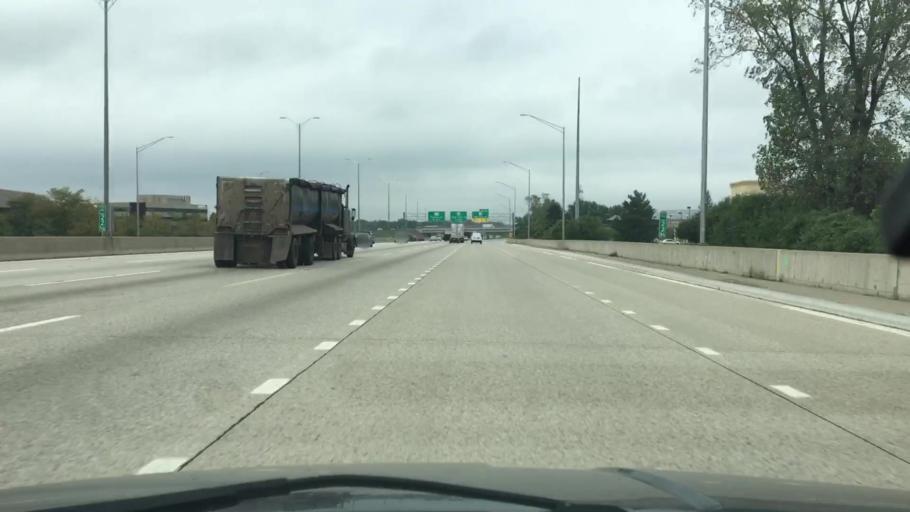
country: US
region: Illinois
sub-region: Lake County
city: Bannockburn
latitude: 42.1948
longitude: -87.8845
